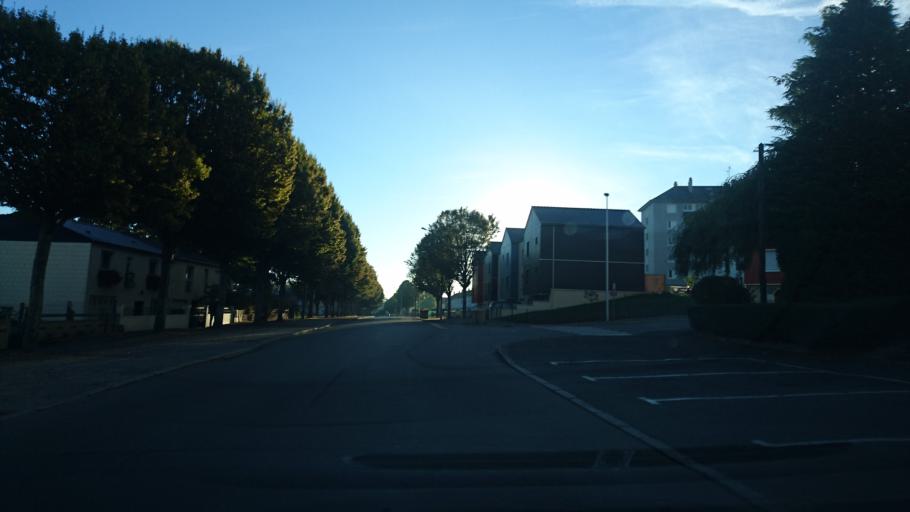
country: FR
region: Brittany
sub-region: Departement d'Ille-et-Vilaine
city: Redon
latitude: 47.6589
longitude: -2.0783
